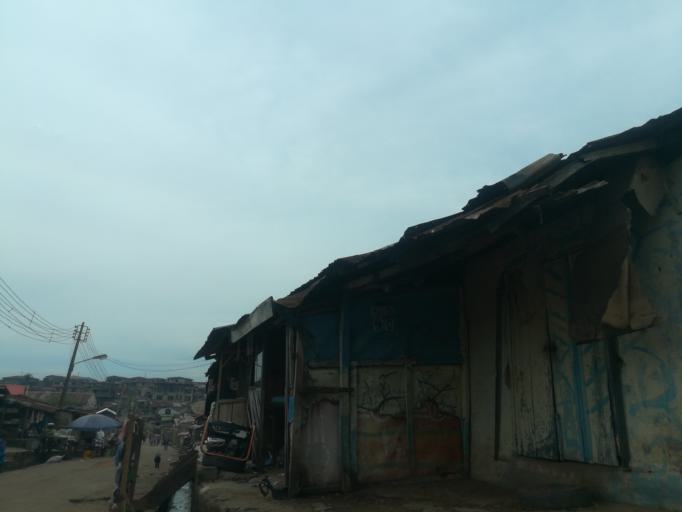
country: NG
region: Oyo
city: Ibadan
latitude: 7.3763
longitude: 3.9323
